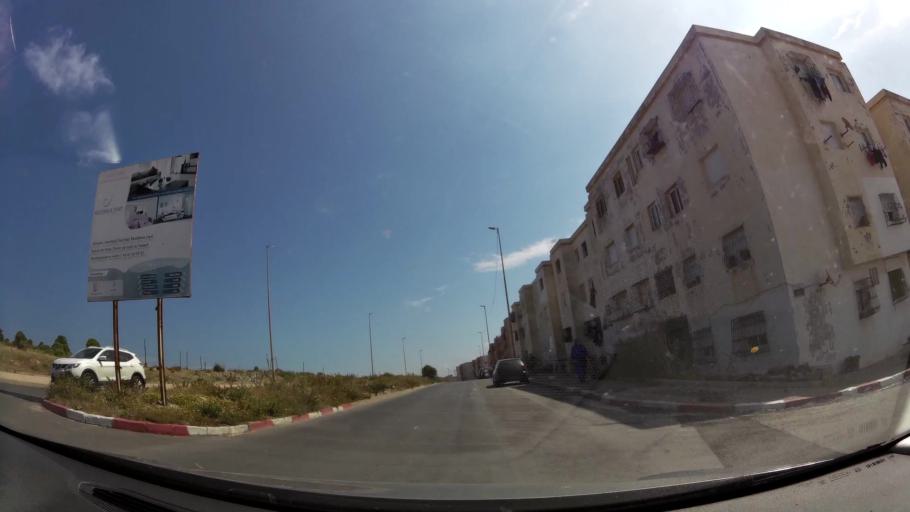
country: MA
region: Rabat-Sale-Zemmour-Zaer
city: Sale
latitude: 34.0793
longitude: -6.7932
